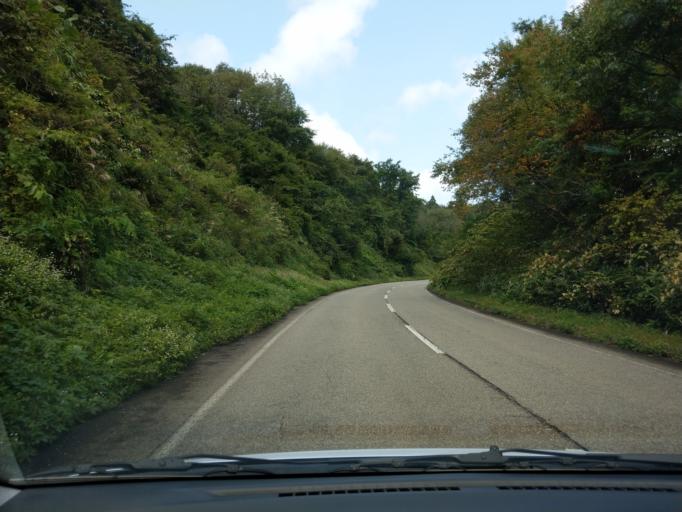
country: JP
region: Akita
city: Omagari
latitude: 39.4744
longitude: 140.3093
